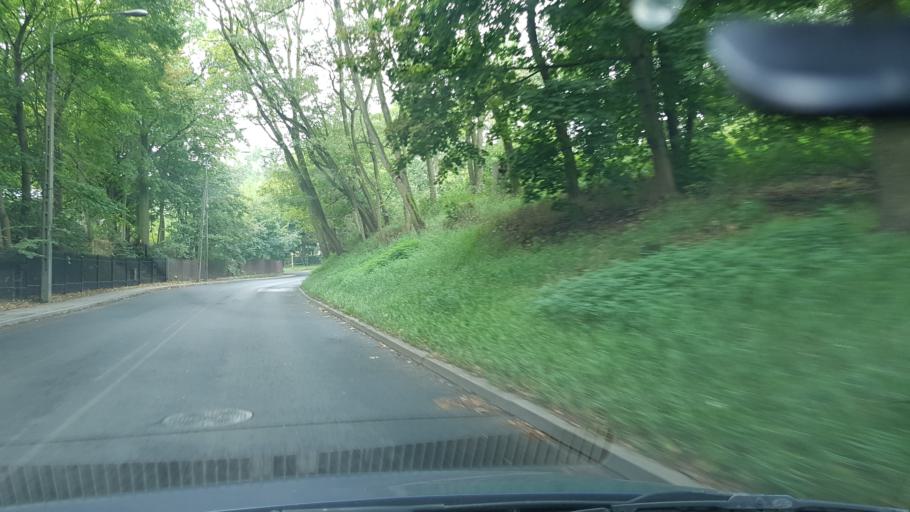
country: PL
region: Masovian Voivodeship
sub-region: Powiat piaseczynski
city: Konstancin-Jeziorna
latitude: 52.1058
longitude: 21.1034
